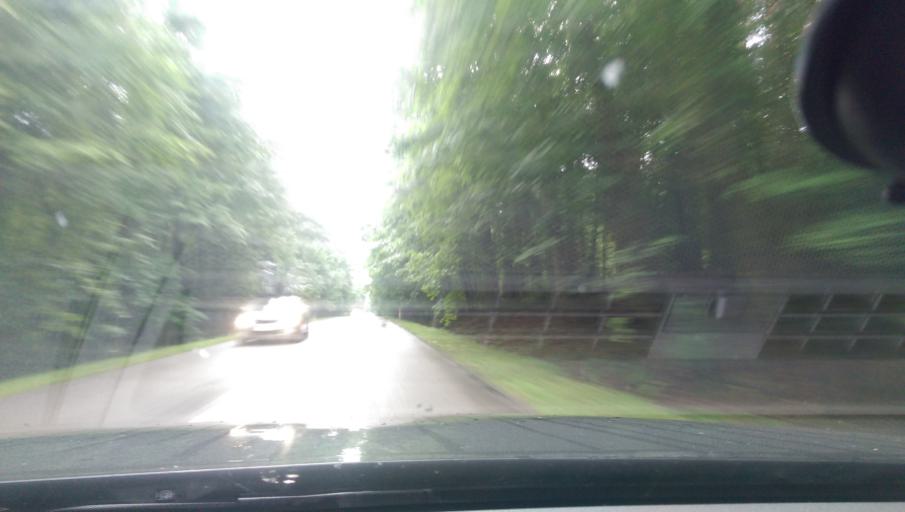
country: PL
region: Warmian-Masurian Voivodeship
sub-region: Powiat mragowski
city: Piecki
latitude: 53.7130
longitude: 21.4318
